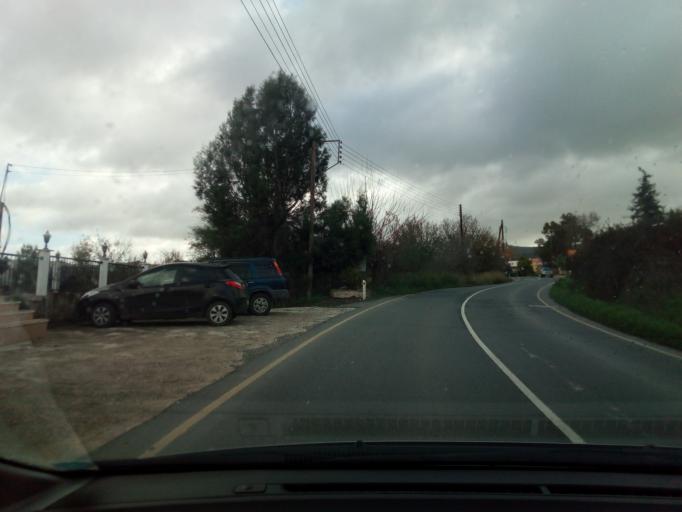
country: CY
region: Pafos
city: Tala
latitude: 34.9235
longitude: 32.4782
